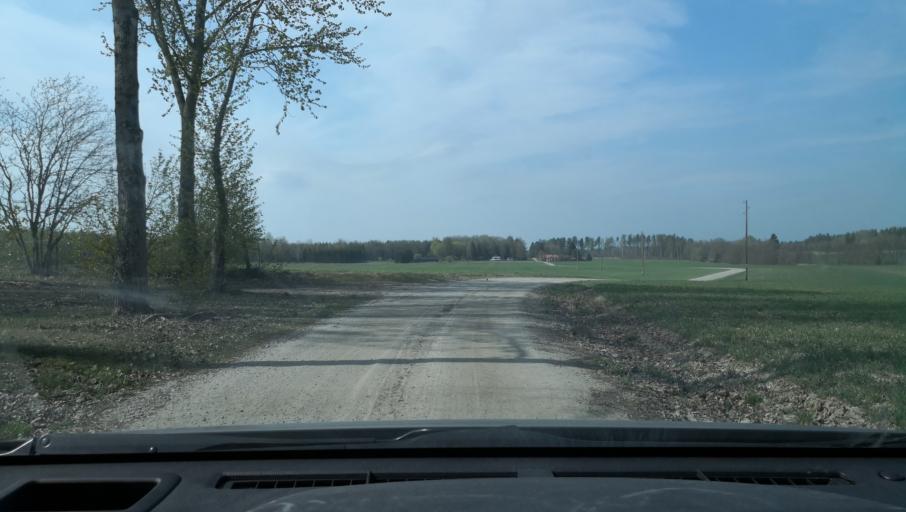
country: SE
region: Vaestmanland
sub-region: Vasteras
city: Skultuna
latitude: 59.7757
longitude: 16.4246
